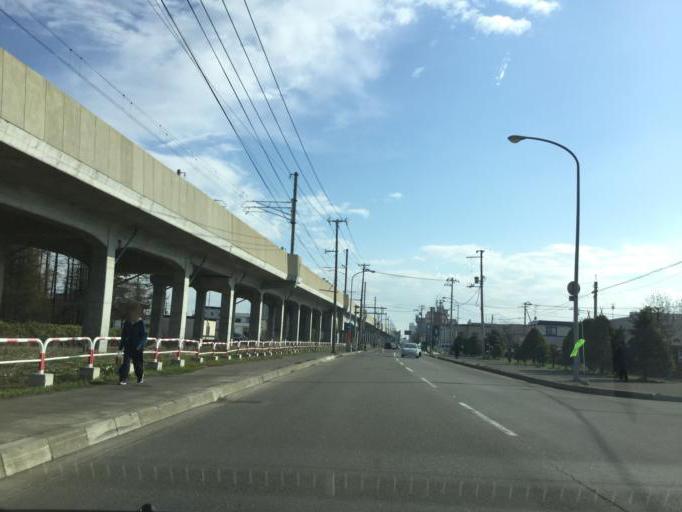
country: JP
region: Hokkaido
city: Ebetsu
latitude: 43.0883
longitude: 141.5242
